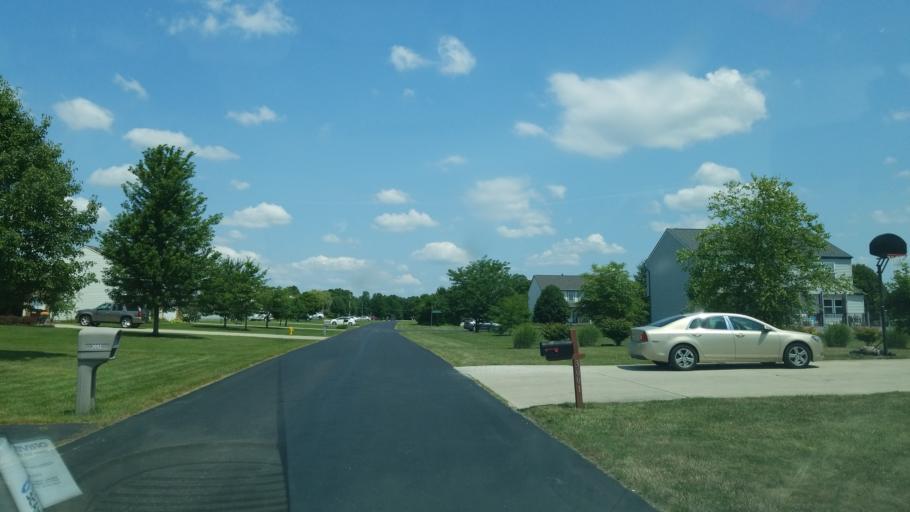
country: US
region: Ohio
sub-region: Delaware County
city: Lewis Center
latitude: 40.2362
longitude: -82.9923
